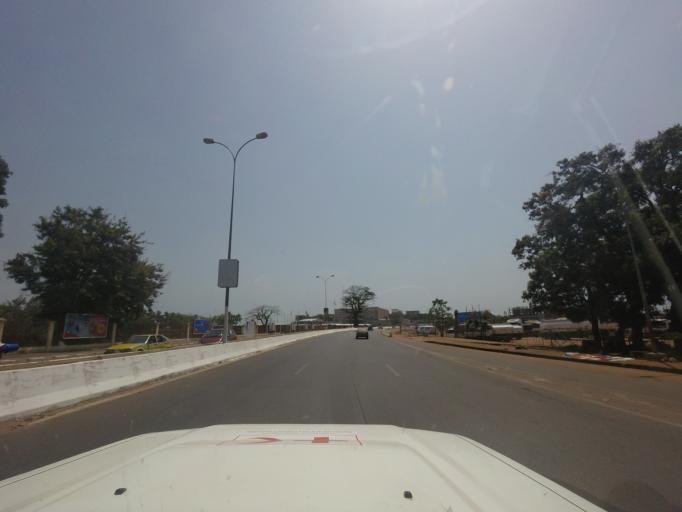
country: GN
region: Conakry
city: Camayenne
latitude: 9.5226
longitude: -13.6905
